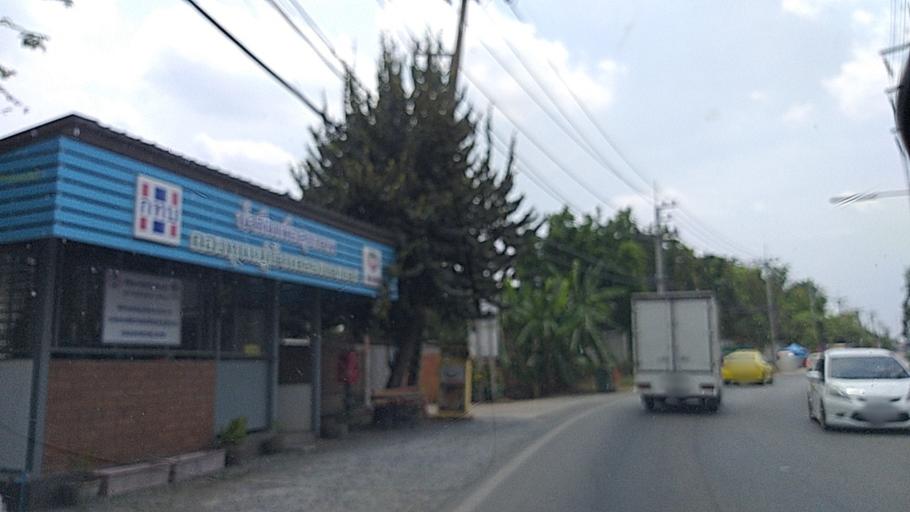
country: TH
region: Bangkok
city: Thawi Watthana
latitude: 13.7527
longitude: 100.2813
